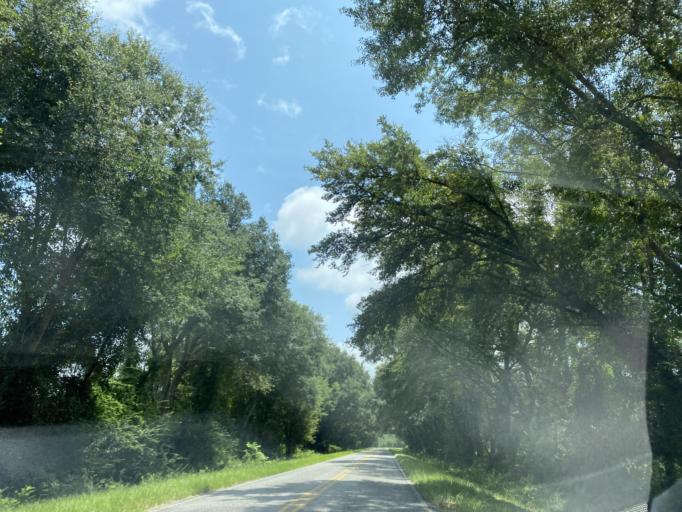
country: US
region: Georgia
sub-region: Telfair County
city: Lumber City
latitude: 32.0029
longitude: -82.7152
